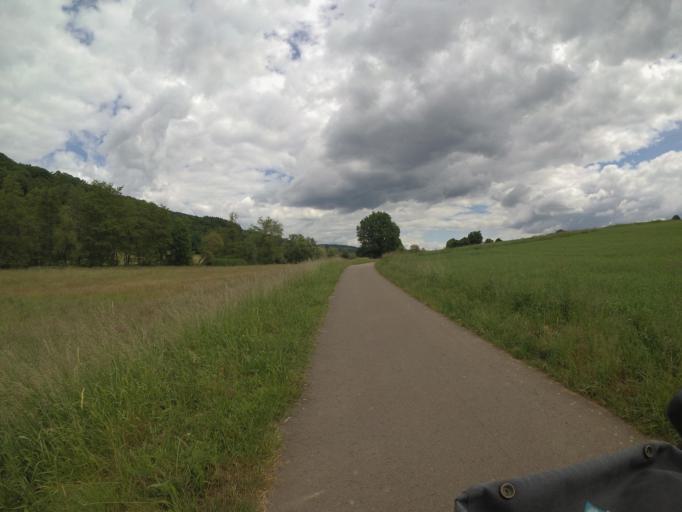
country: DE
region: Rheinland-Pfalz
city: Ulmet
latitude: 49.5898
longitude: 7.4479
